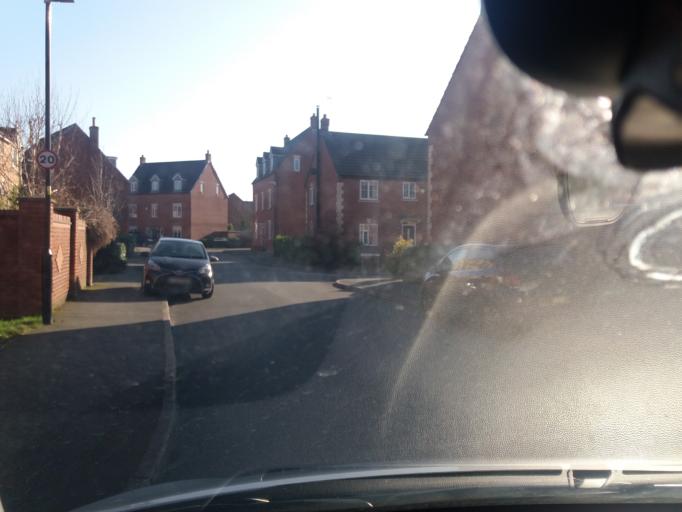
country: GB
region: England
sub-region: Lancashire
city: Adlington
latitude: 53.6192
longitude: -2.6075
